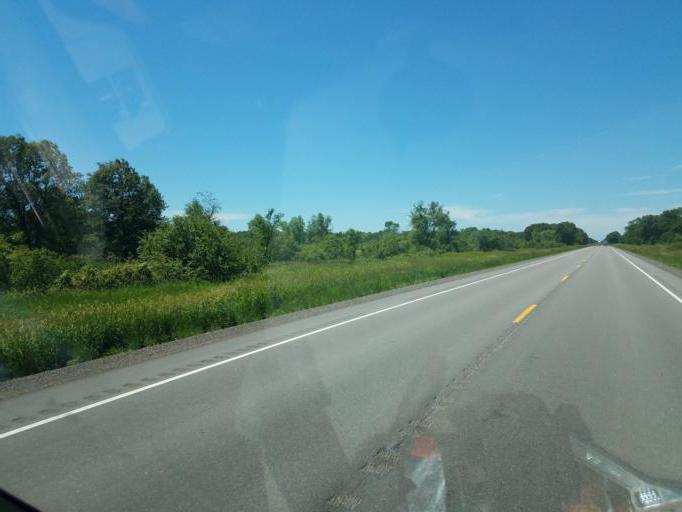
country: US
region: Wisconsin
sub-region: Juneau County
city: New Lisbon
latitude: 44.0258
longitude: -90.2579
